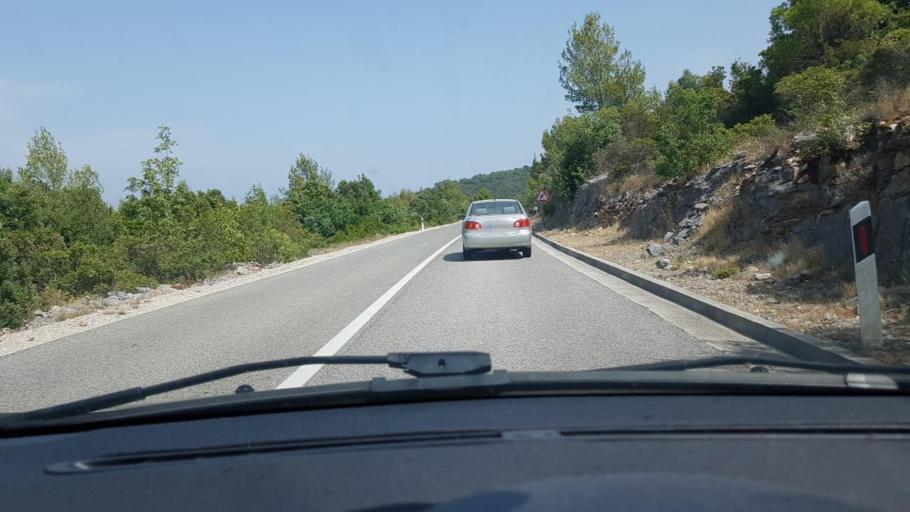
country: HR
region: Dubrovacko-Neretvanska
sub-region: Grad Korcula
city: Zrnovo
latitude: 42.9388
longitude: 17.0769
